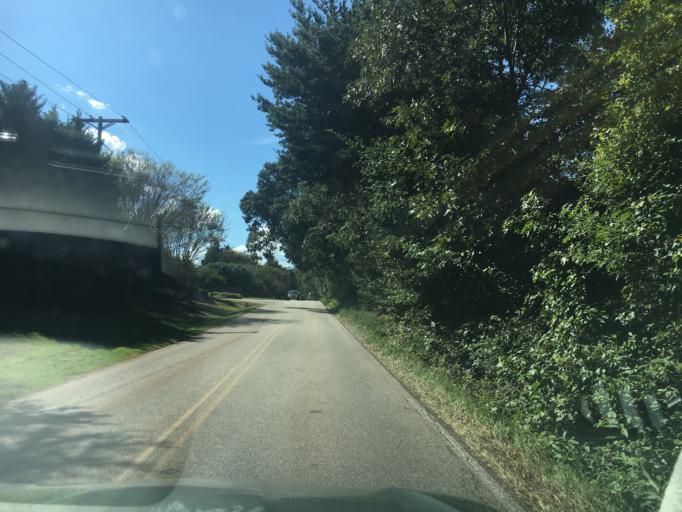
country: US
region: South Carolina
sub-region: Greenville County
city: Five Forks
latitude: 34.8217
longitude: -82.2228
